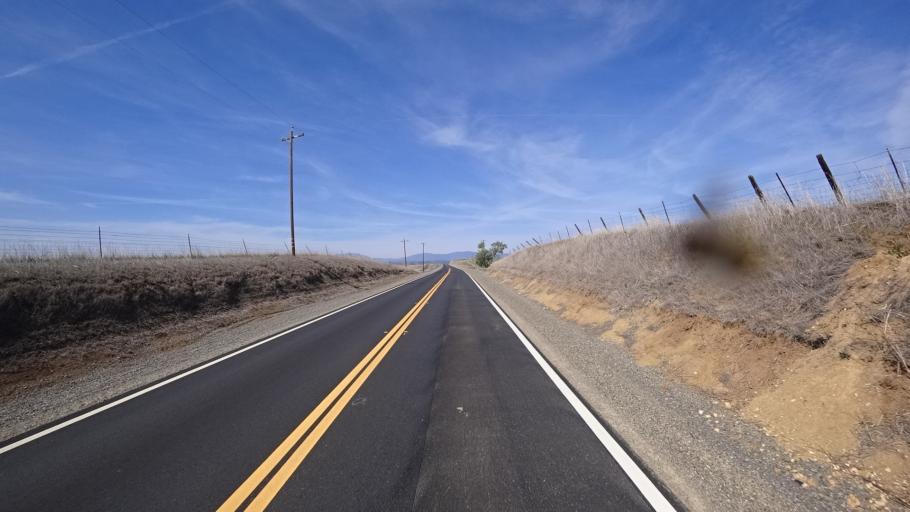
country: US
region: California
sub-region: Glenn County
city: Willows
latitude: 39.5315
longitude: -122.3191
